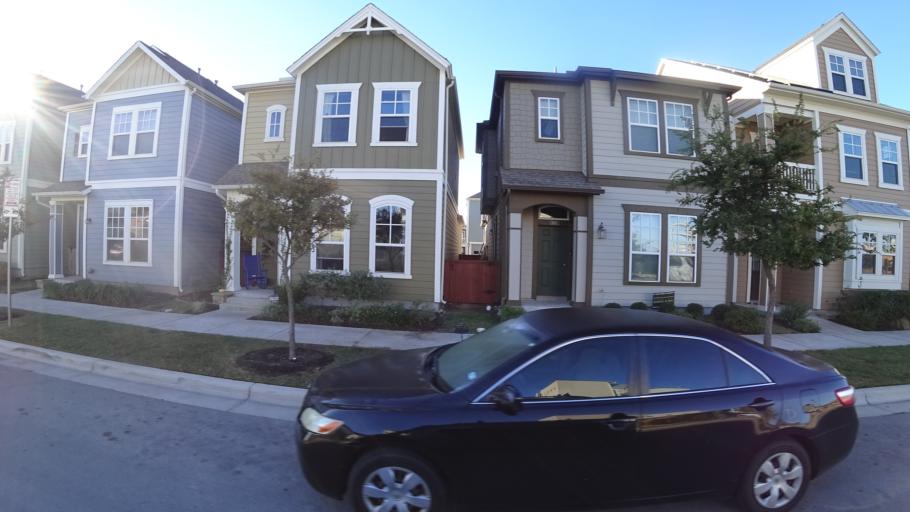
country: US
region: Texas
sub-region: Travis County
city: Austin
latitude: 30.2999
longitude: -97.7018
